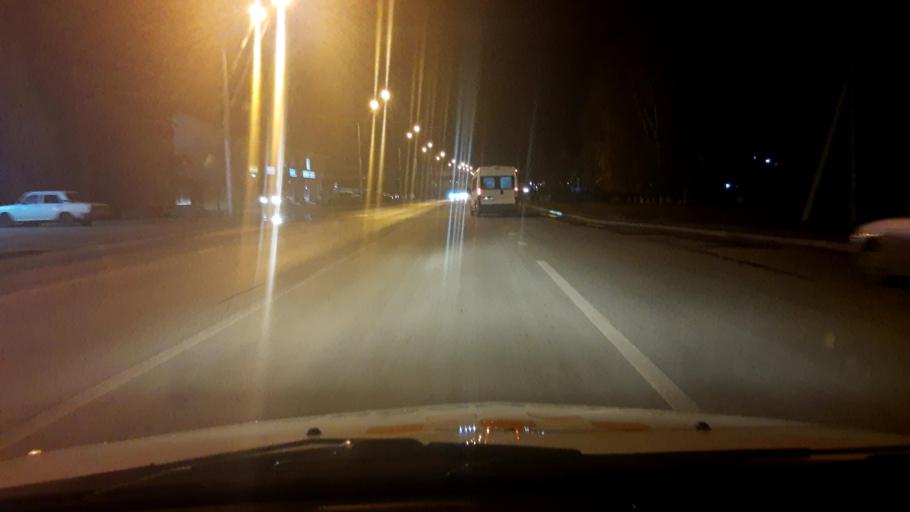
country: RU
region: Bashkortostan
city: Iglino
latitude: 54.7649
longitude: 56.2378
